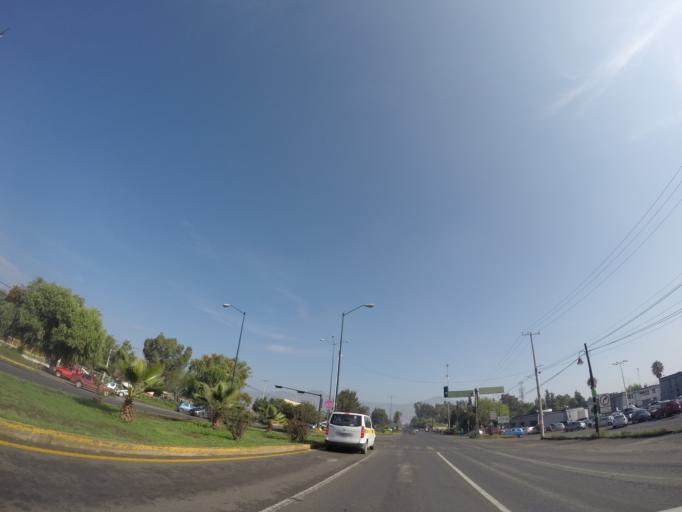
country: MX
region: Michoacan
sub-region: Morelia
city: Morelos
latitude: 19.6808
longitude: -101.2351
